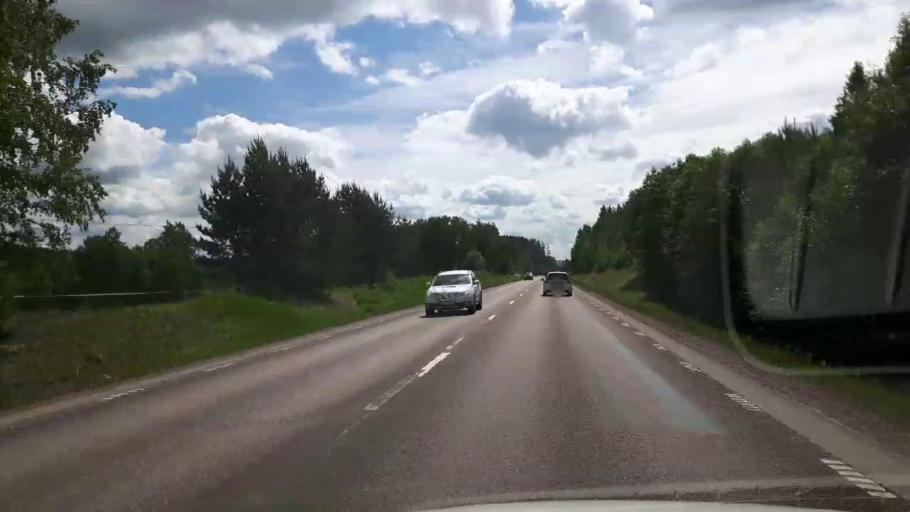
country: SE
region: Dalarna
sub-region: Saters Kommun
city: Saeter
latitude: 60.4601
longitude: 15.8022
